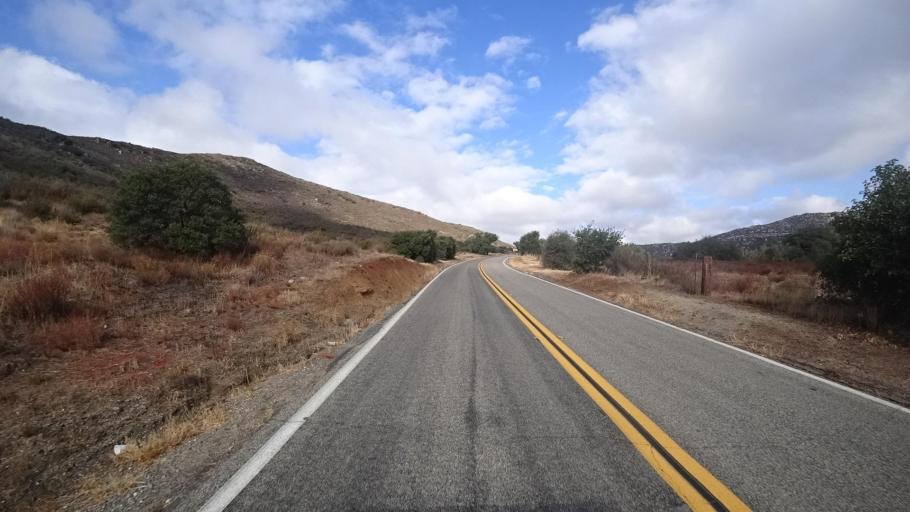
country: MX
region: Baja California
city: Tecate
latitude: 32.6224
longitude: -116.6202
